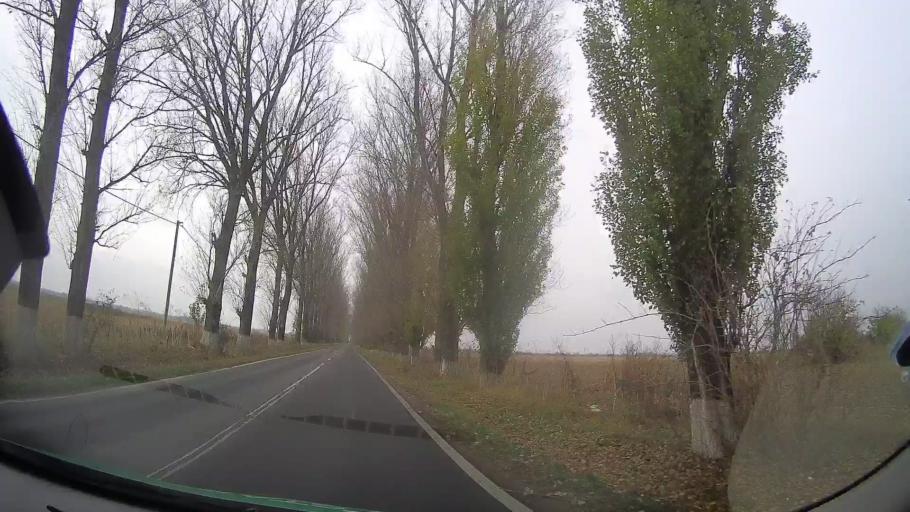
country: RO
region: Ilfov
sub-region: Comuna Gruiu
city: Gruiu
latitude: 44.7406
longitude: 26.2085
